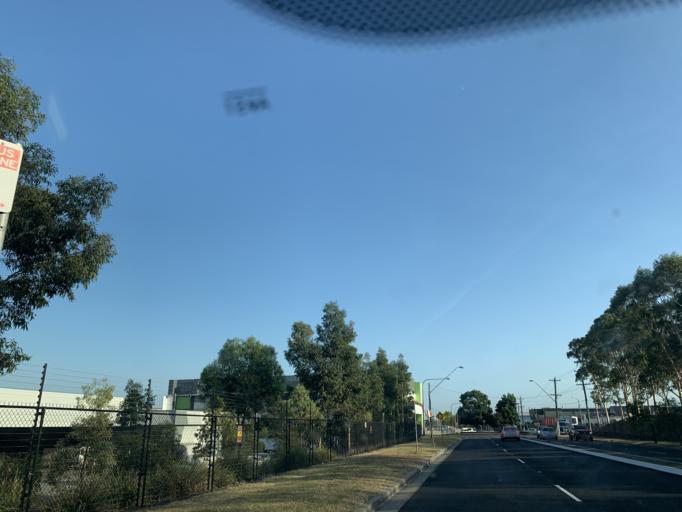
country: AU
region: New South Wales
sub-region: Blacktown
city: Doonside
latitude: -33.7974
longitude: 150.8707
